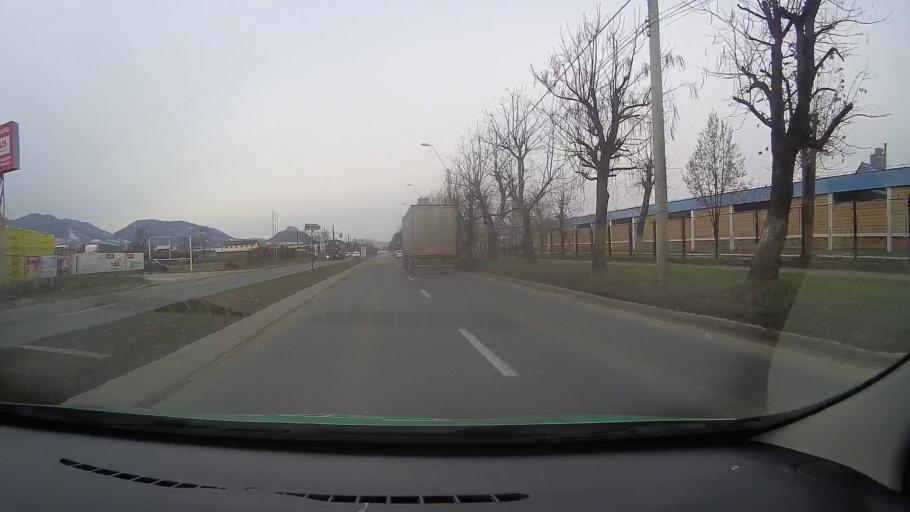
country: RO
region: Hunedoara
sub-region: Municipiul Deva
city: Deva
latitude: 45.8649
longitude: 22.9242
